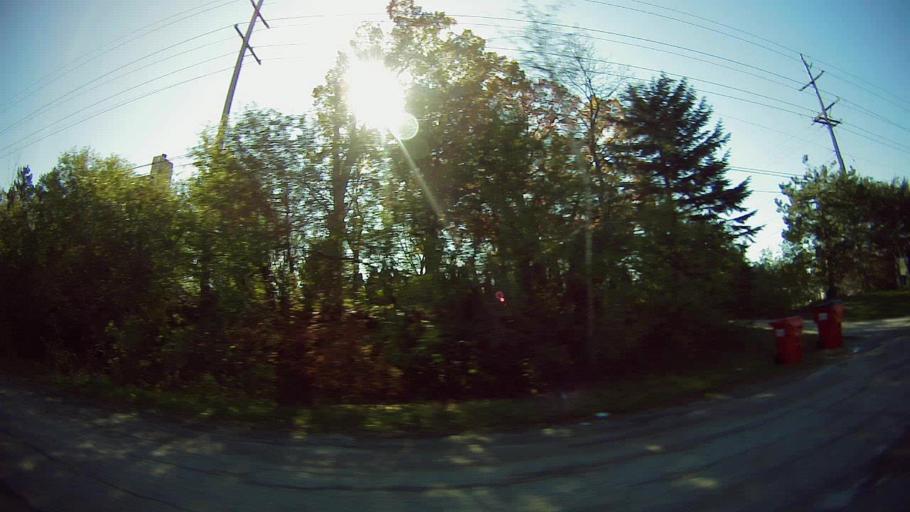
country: US
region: Michigan
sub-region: Oakland County
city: Franklin
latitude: 42.5435
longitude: -83.3400
